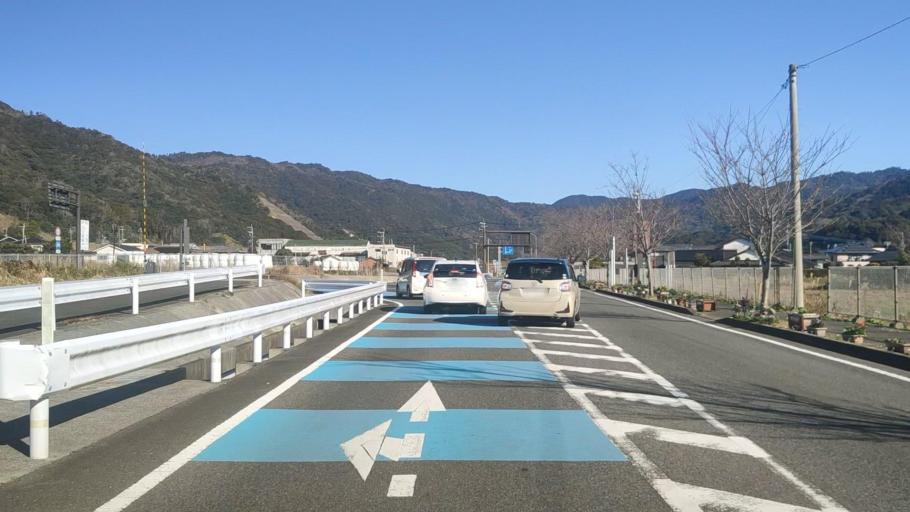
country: JP
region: Miyazaki
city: Nobeoka
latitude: 32.7097
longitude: 131.8197
